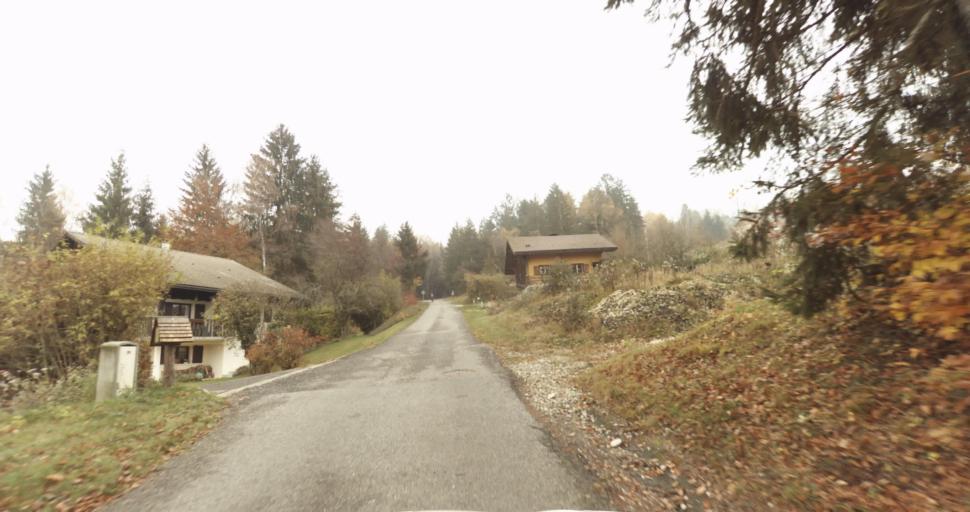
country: FR
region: Rhone-Alpes
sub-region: Departement de la Haute-Savoie
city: Viuz-la-Chiesaz
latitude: 45.8082
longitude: 6.0702
